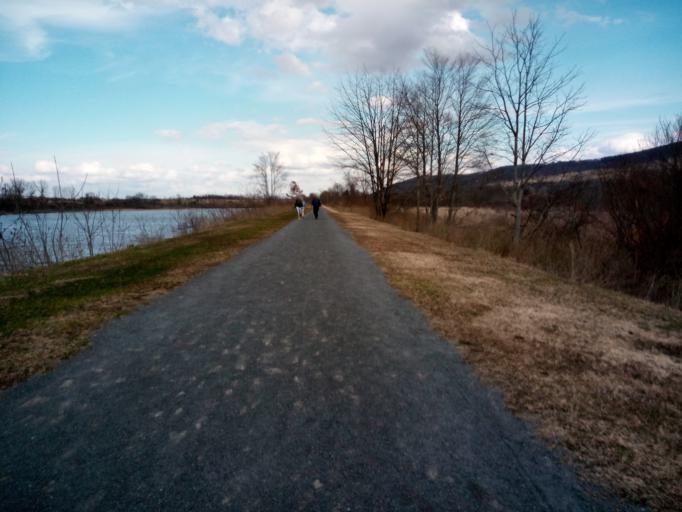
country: US
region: New York
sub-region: Chemung County
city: Big Flats
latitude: 42.1423
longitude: -76.9208
